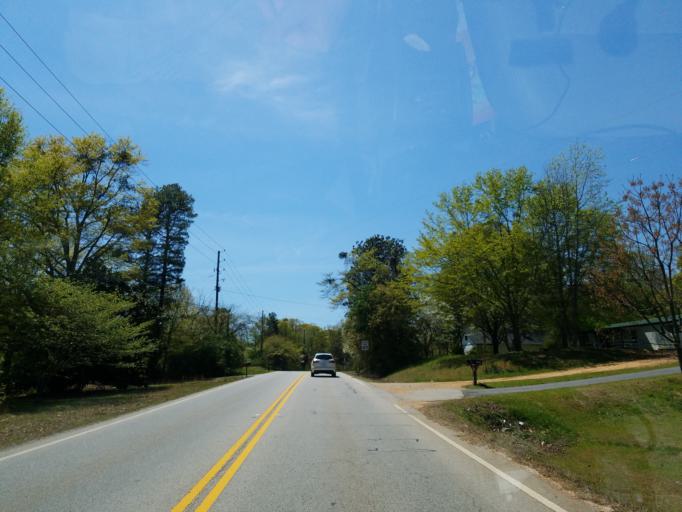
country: US
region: Georgia
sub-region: Paulding County
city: Hiram
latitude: 33.8660
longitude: -84.7990
